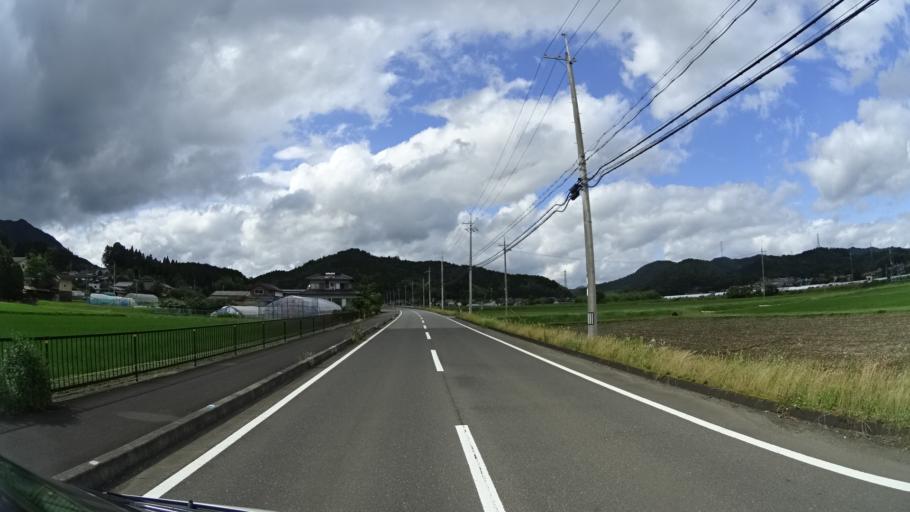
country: JP
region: Kyoto
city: Ayabe
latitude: 35.3265
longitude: 135.2079
